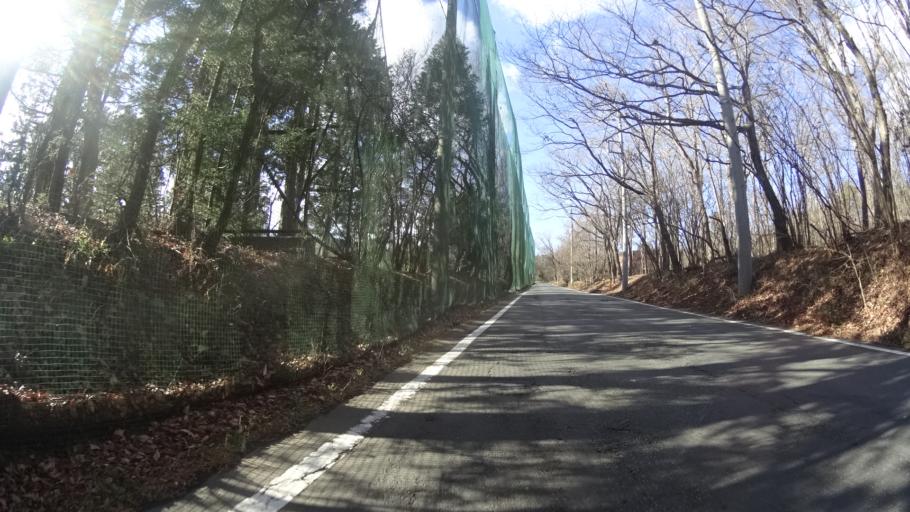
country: JP
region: Shizuoka
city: Gotemba
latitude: 35.3462
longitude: 138.8839
